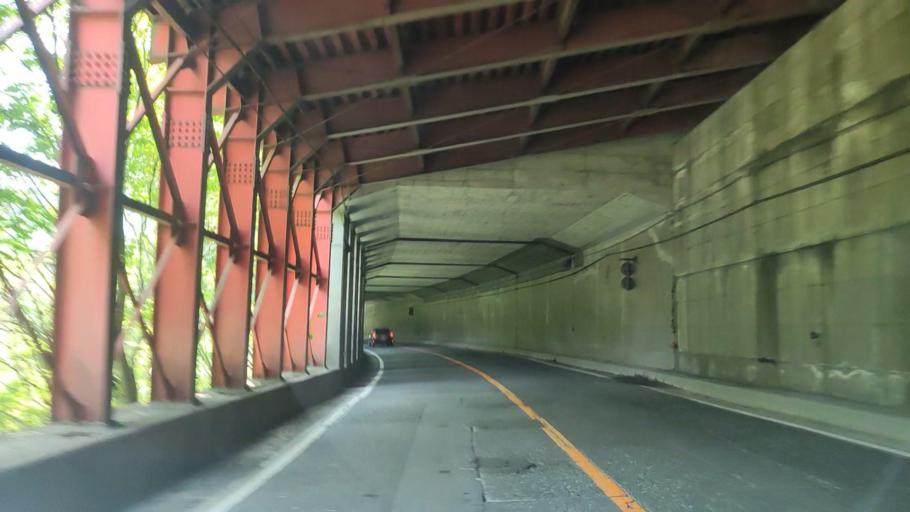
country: JP
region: Niigata
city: Itoigawa
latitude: 36.9153
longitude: 137.8649
